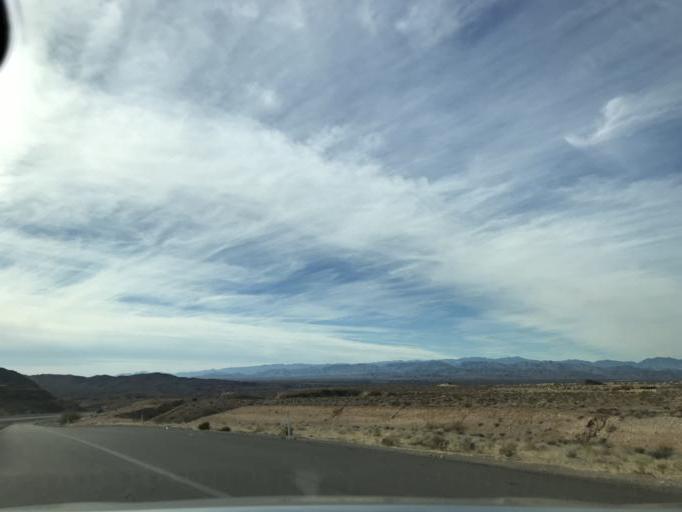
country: US
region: Nevada
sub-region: Clark County
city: Moapa Town
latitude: 36.6716
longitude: -114.5223
